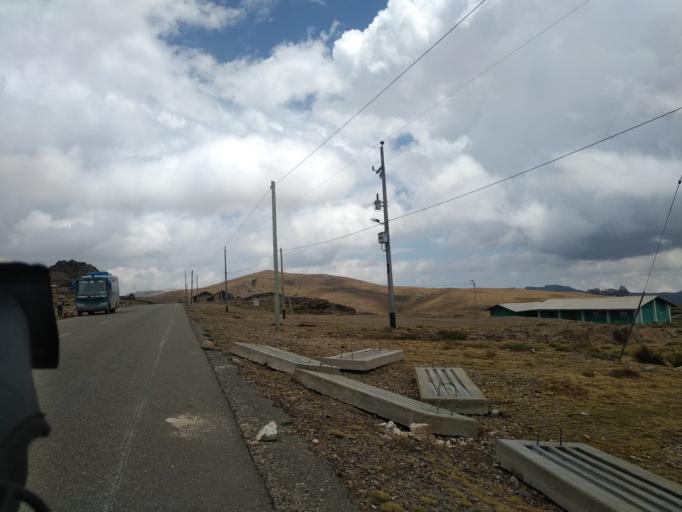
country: PE
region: La Libertad
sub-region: Provincia de Santiago de Chuco
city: Quiruvilca
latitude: -7.9745
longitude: -78.2125
